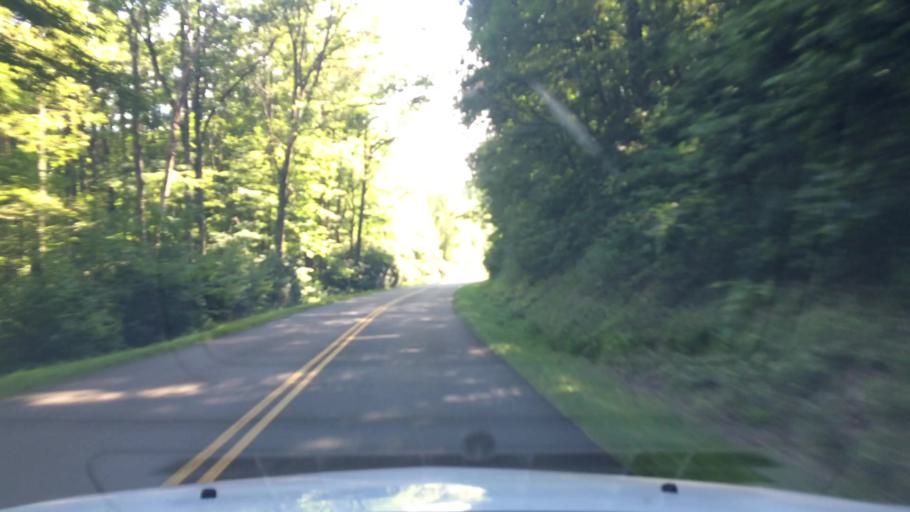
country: US
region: North Carolina
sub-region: Watauga County
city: Foscoe
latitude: 36.1342
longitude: -81.7418
